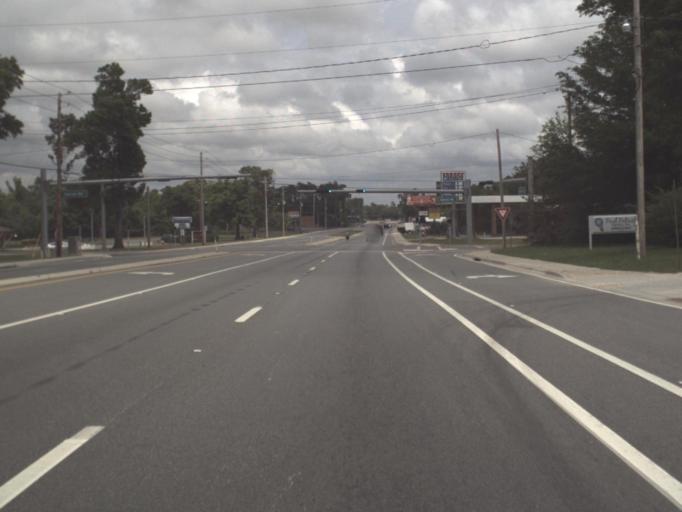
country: US
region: Florida
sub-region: Santa Rosa County
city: Bagdad
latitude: 30.5944
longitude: -87.0799
